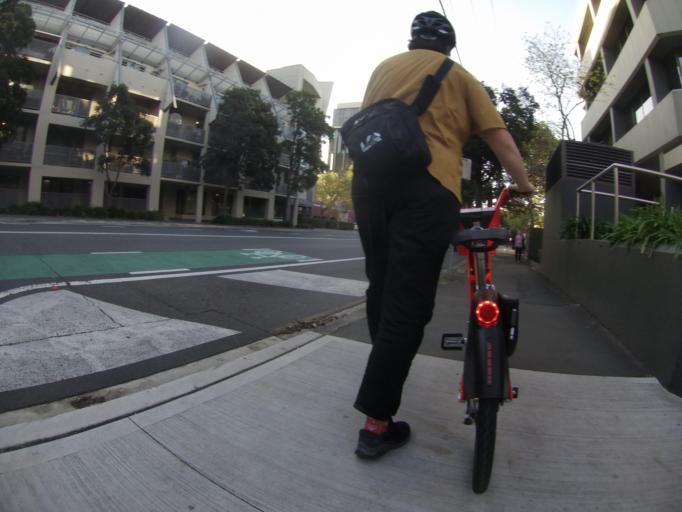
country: AU
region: New South Wales
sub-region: Marrickville
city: Camperdown
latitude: -33.8919
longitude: 151.1830
